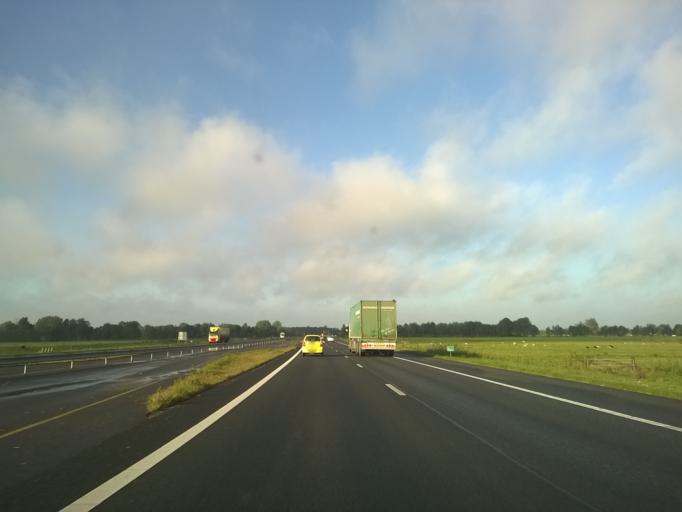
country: NL
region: Groningen
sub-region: Gemeente Zuidhorn
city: Aduard
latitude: 53.1965
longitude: 6.4429
